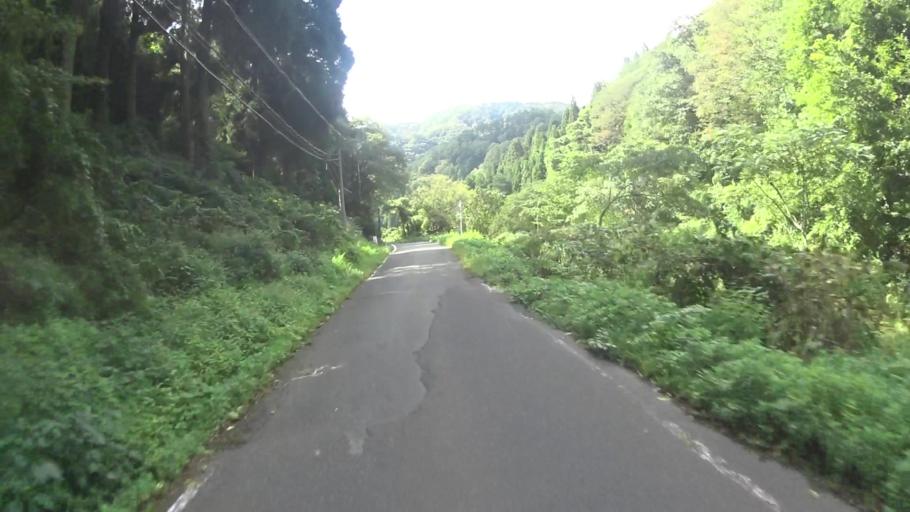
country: JP
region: Kyoto
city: Miyazu
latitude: 35.7002
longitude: 135.1836
